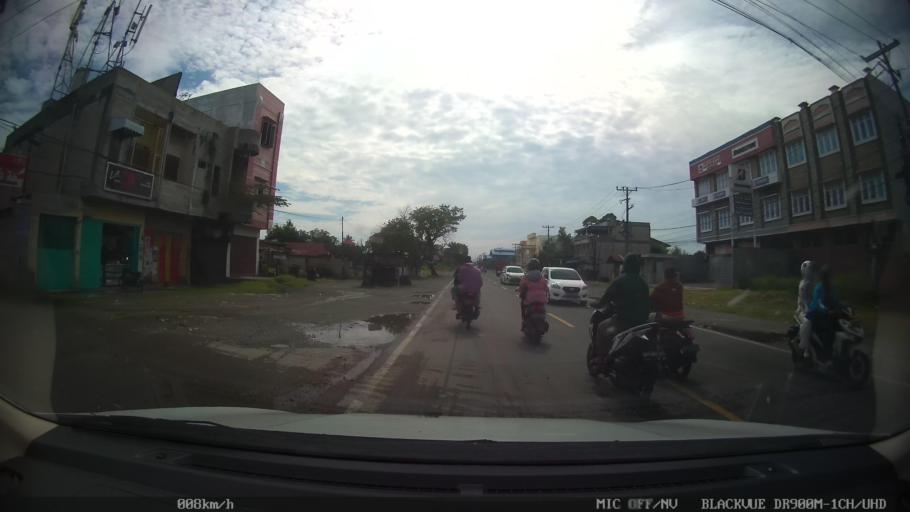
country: ID
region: North Sumatra
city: Medan
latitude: 3.6164
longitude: 98.6453
